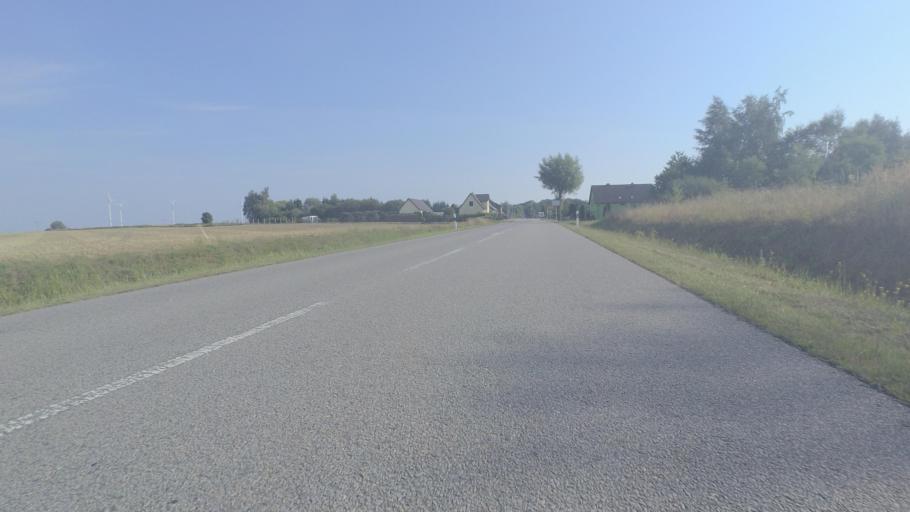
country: DE
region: Mecklenburg-Vorpommern
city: Grimmen
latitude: 54.1323
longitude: 13.0536
